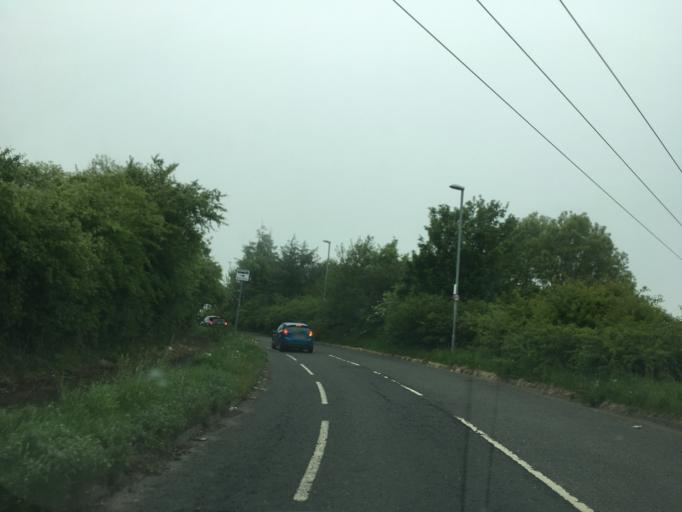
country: GB
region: Scotland
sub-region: Midlothian
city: Penicuik
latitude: 55.8517
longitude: -3.1905
